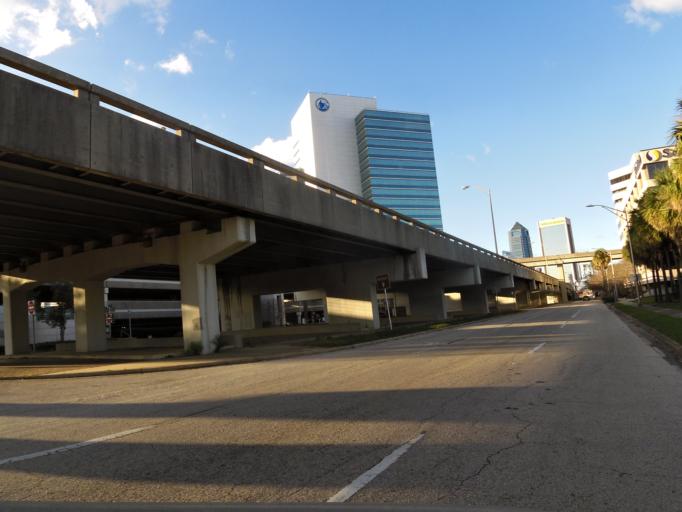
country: US
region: Florida
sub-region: Duval County
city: Jacksonville
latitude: 30.2768
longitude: -81.6564
